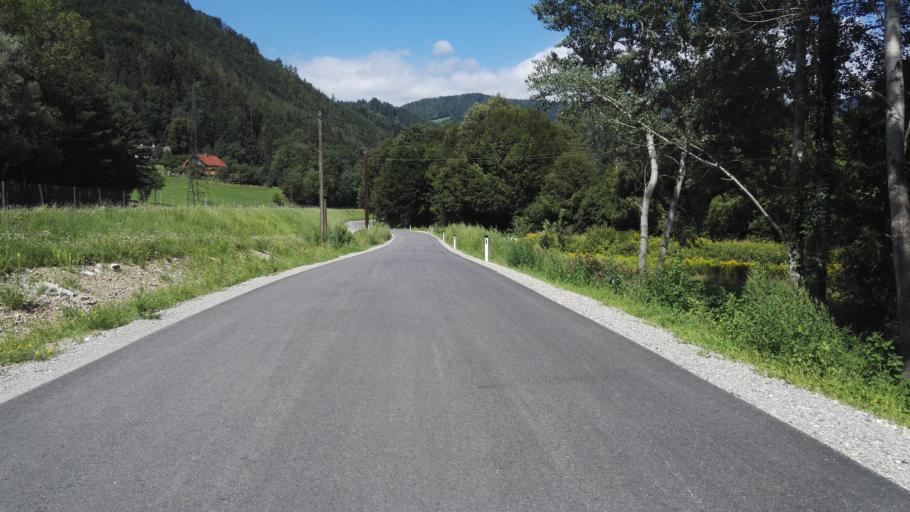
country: AT
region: Styria
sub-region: Politischer Bezirk Graz-Umgebung
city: Peggau
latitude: 47.2275
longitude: 15.3297
